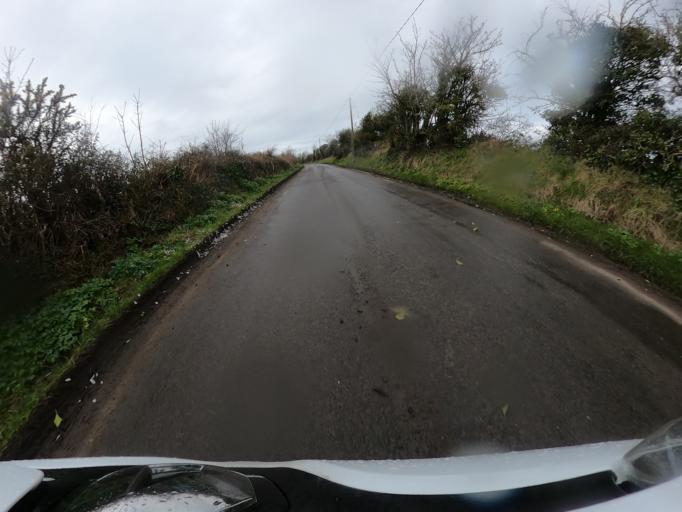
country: IM
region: Ramsey
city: Ramsey
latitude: 54.3785
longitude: -4.4548
